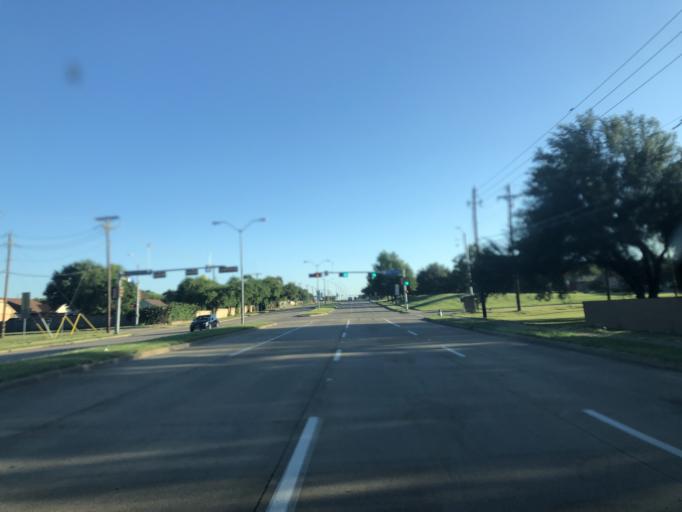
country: US
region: Texas
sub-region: Dallas County
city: Duncanville
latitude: 32.6414
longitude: -96.9427
